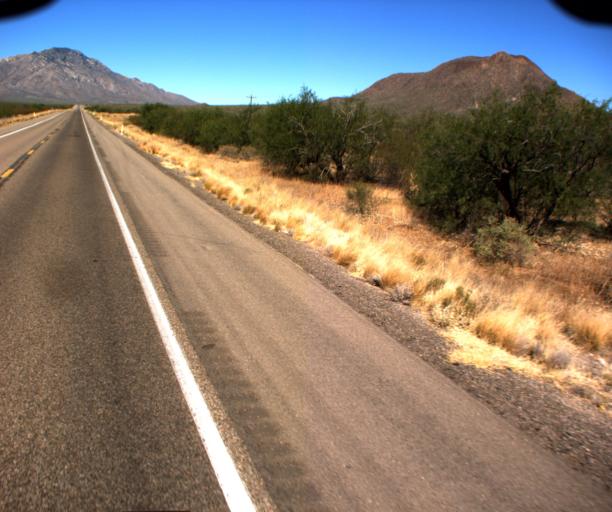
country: US
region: Arizona
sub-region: Pima County
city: Three Points
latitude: 32.0526
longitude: -111.4149
